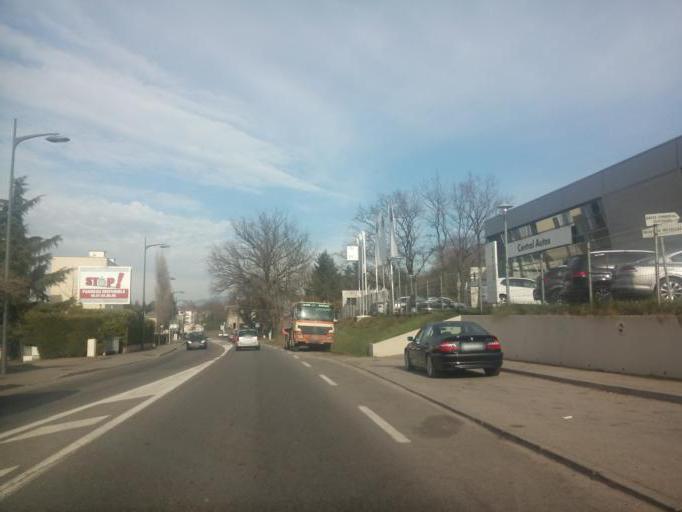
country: FR
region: Rhone-Alpes
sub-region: Departement du Rhone
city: Francheville
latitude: 45.7469
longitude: 4.7723
